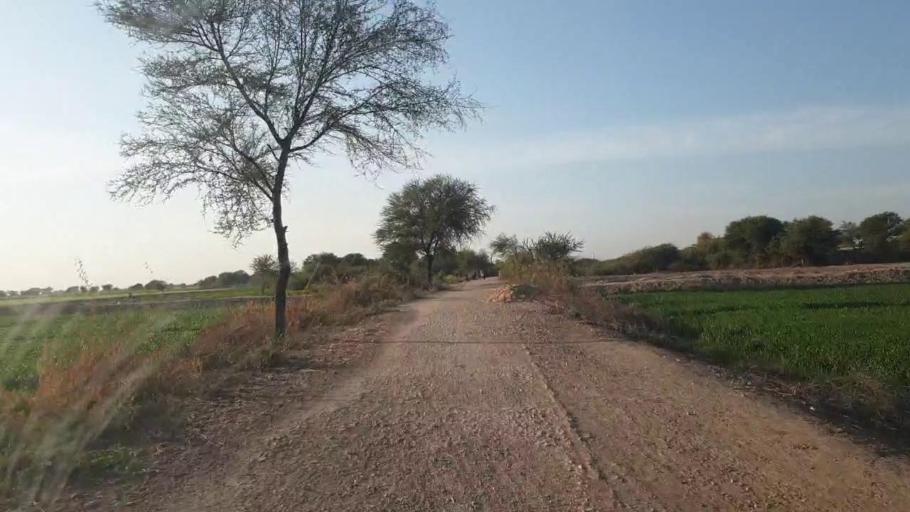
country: PK
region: Sindh
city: Chambar
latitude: 25.2829
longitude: 68.8022
